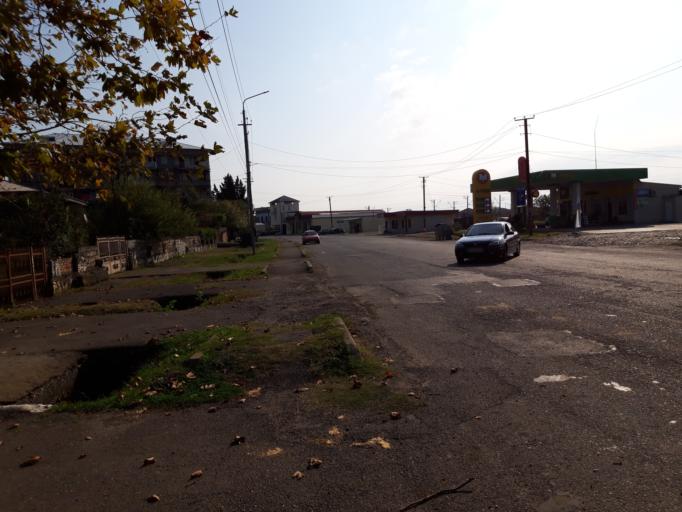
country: GE
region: Imereti
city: Samtredia
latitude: 42.1591
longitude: 42.3284
